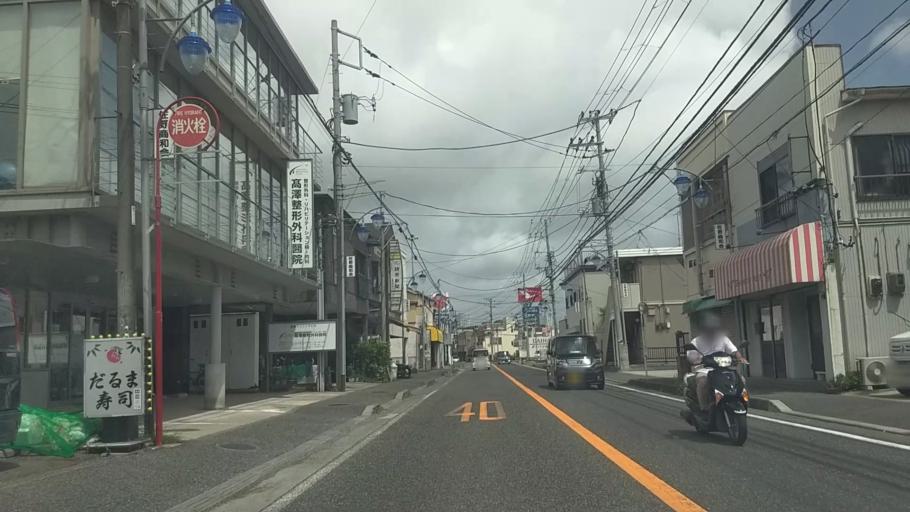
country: JP
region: Kanagawa
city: Yokosuka
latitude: 35.2618
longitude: 139.6689
